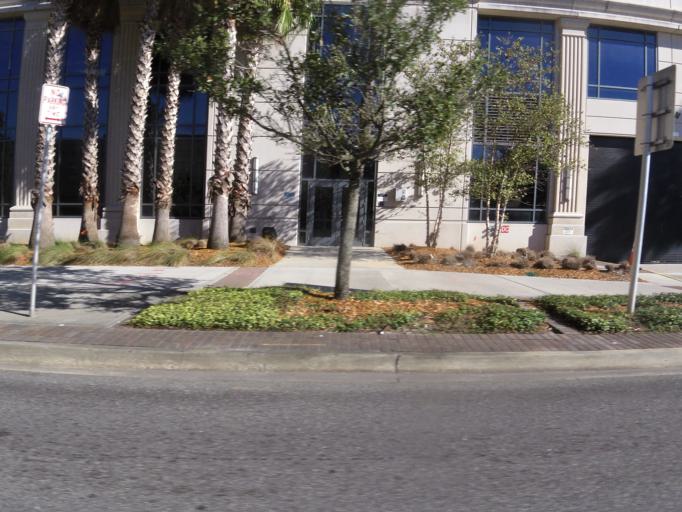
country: US
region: Florida
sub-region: Duval County
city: Jacksonville
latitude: 30.3304
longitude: -81.6645
